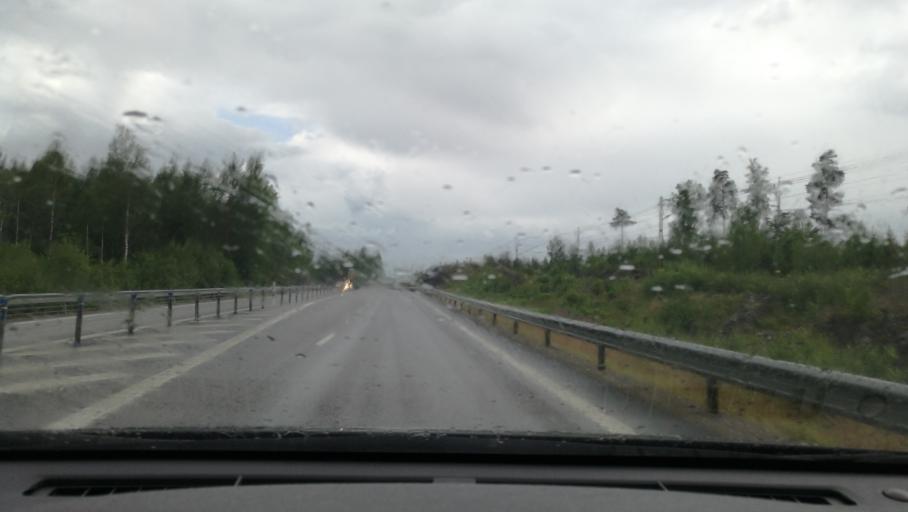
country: SE
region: OEstergoetland
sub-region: Norrkopings Kommun
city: Jursla
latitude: 58.8106
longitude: 16.1526
